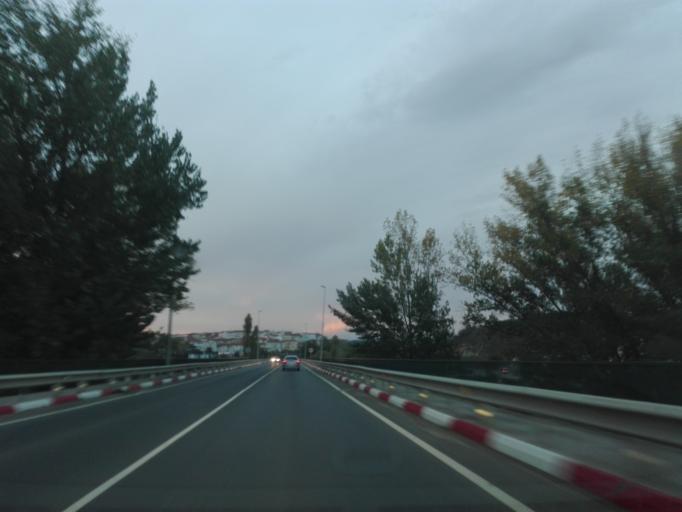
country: ES
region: Extremadura
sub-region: Provincia de Caceres
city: Coria
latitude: 39.9778
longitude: -6.5277
